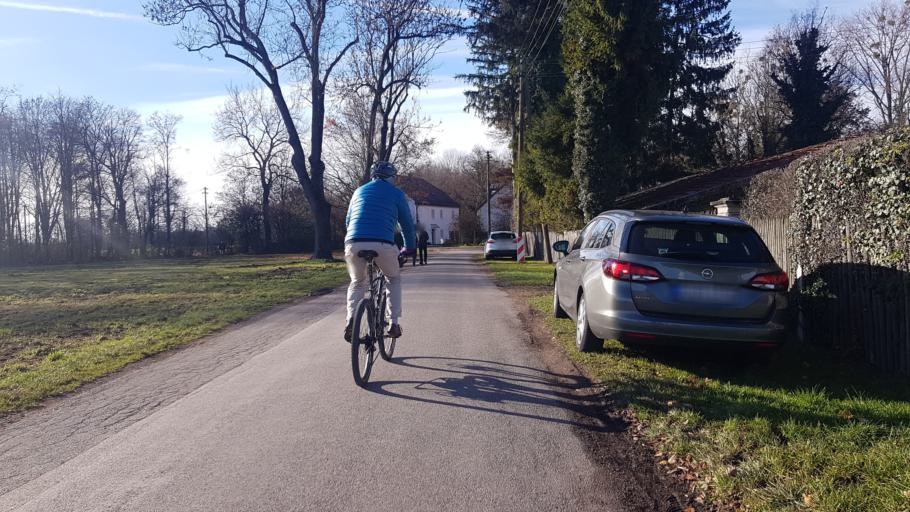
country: DE
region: Bavaria
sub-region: Upper Bavaria
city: Karlsfeld
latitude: 48.2143
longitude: 11.5220
